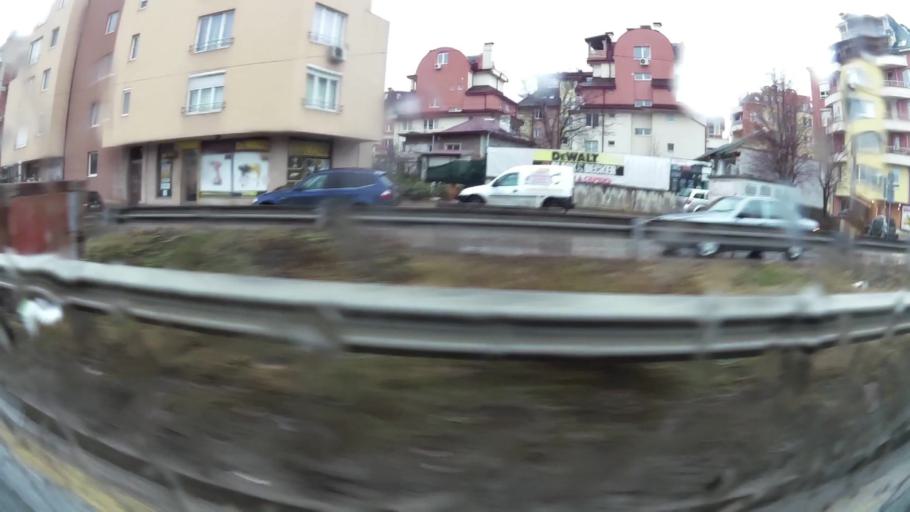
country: BG
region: Sofia-Capital
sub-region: Stolichna Obshtina
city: Sofia
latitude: 42.6500
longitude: 23.3611
